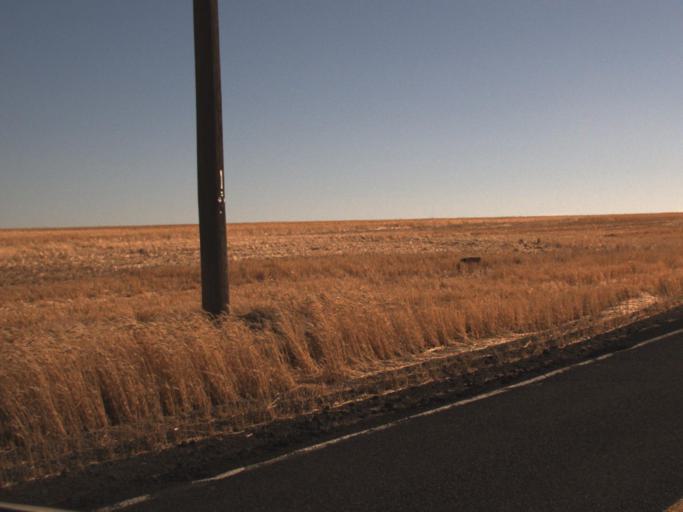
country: US
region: Washington
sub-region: Adams County
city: Ritzville
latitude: 46.9299
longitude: -118.5671
